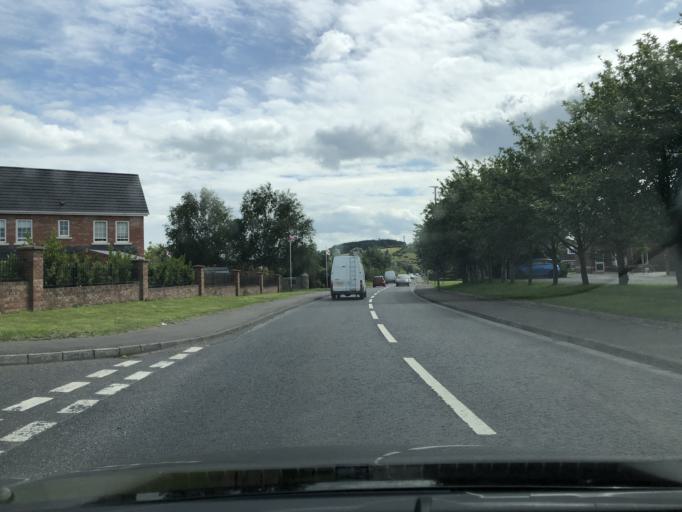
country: GB
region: Northern Ireland
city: Ballynahinch
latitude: 54.4123
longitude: -5.9037
